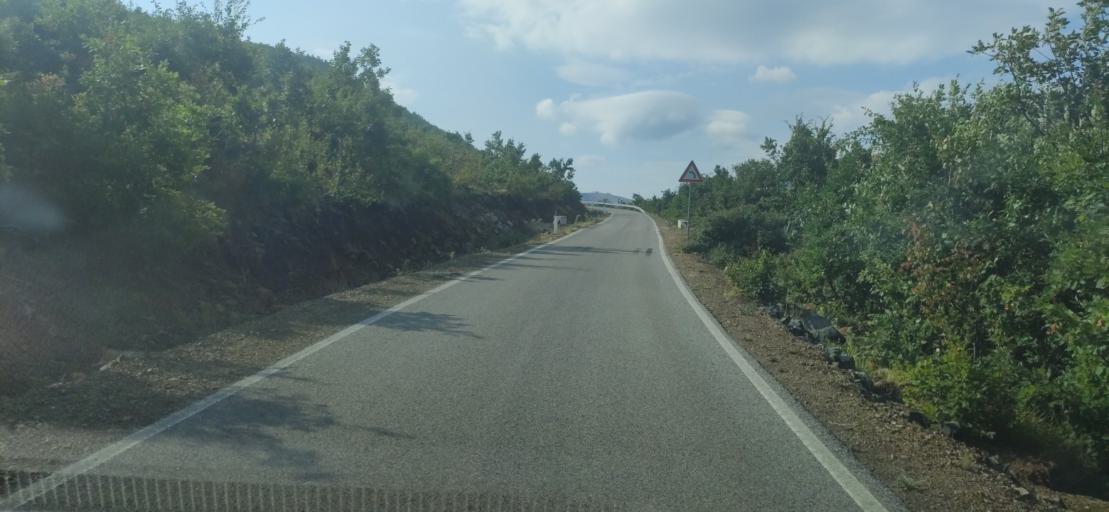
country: AL
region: Shkoder
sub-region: Rrethi i Pukes
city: Iballe
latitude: 42.1731
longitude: 20.0004
